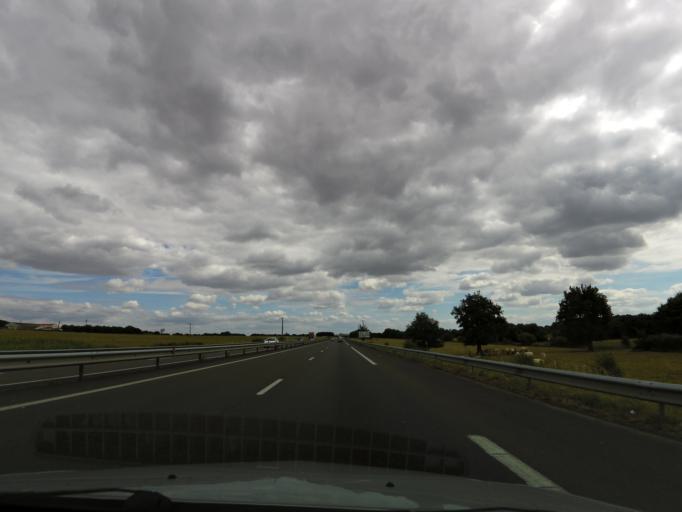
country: FR
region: Pays de la Loire
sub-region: Departement de la Loire-Atlantique
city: Le Bignon
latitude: 47.0832
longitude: -1.4496
